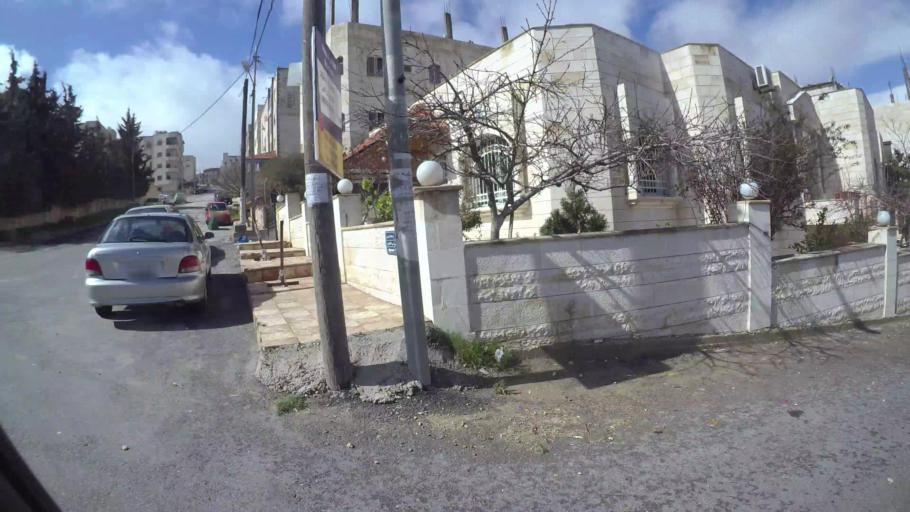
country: JO
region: Amman
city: Al Jubayhah
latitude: 32.0612
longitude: 35.8911
